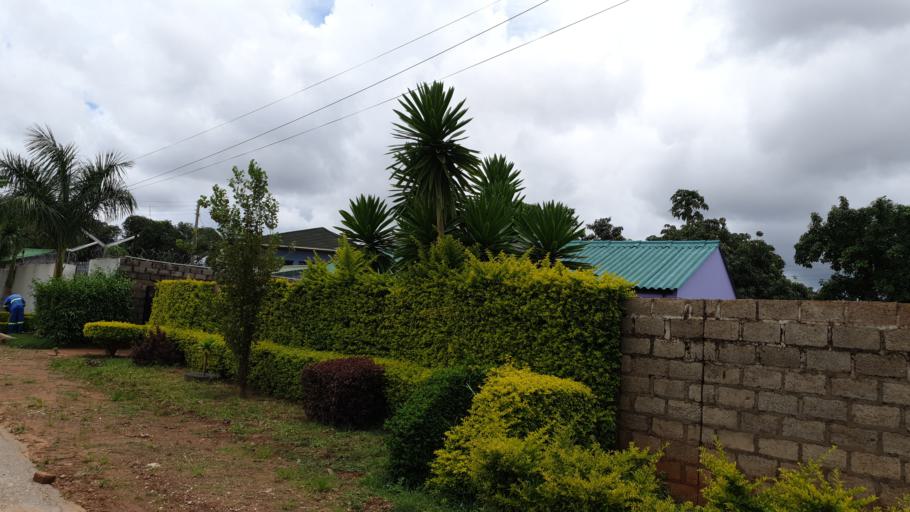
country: ZM
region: Lusaka
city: Lusaka
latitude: -15.4299
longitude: 28.3072
